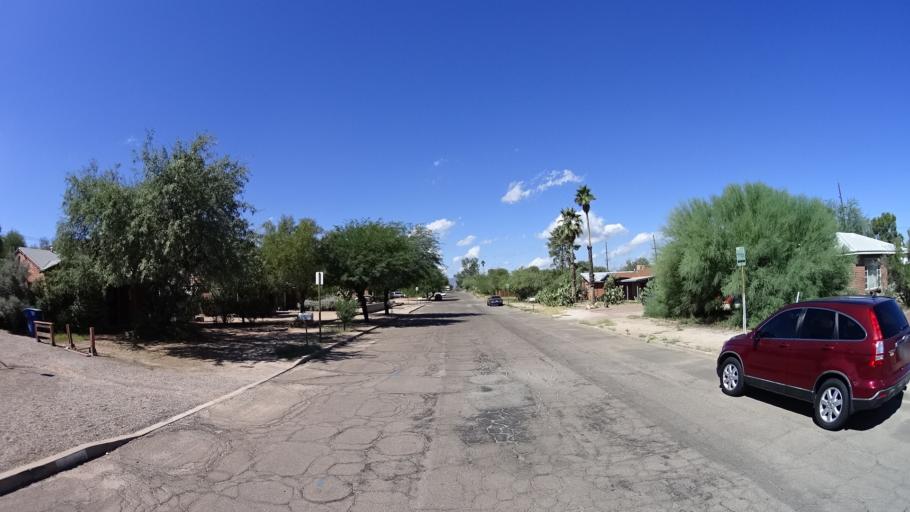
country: US
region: Arizona
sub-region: Pima County
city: Tucson
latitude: 32.2437
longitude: -110.9475
